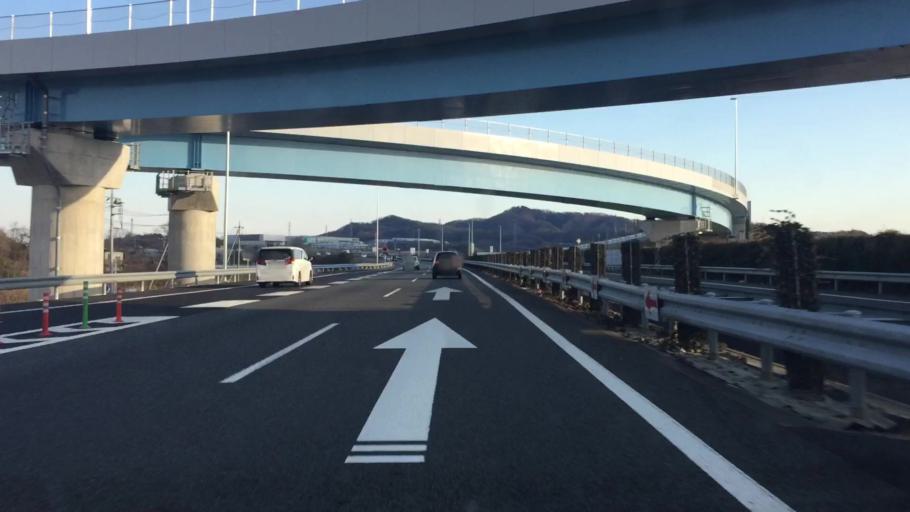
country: JP
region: Gunma
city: Ota
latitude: 36.3389
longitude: 139.3482
